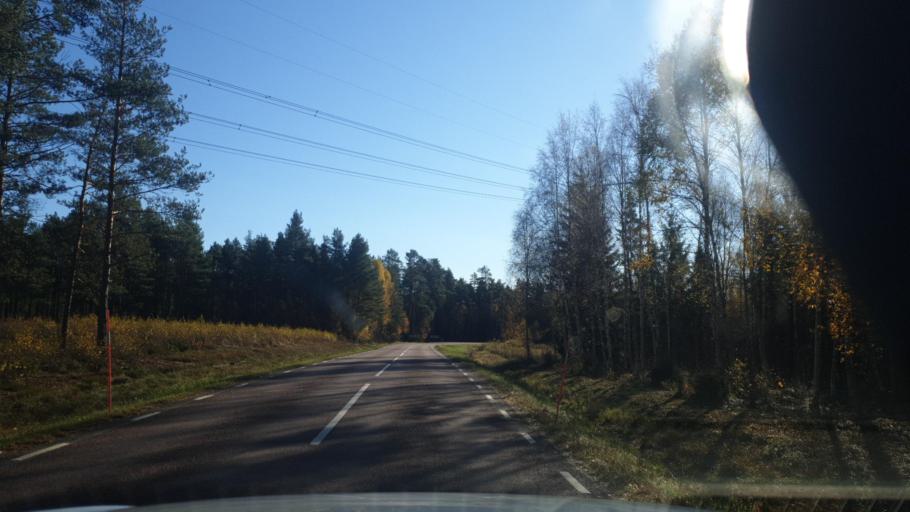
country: SE
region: Vaermland
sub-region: Grums Kommun
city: Grums
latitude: 59.4377
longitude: 12.9785
